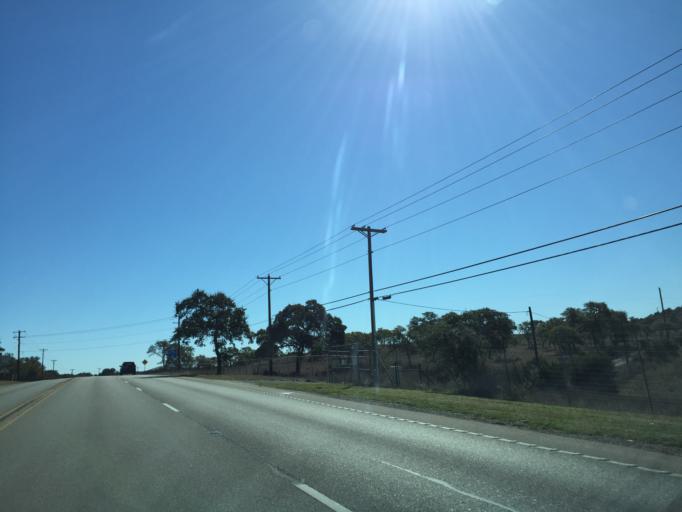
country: US
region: Texas
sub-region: Comal County
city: Canyon Lake
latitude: 29.7839
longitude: -98.3234
